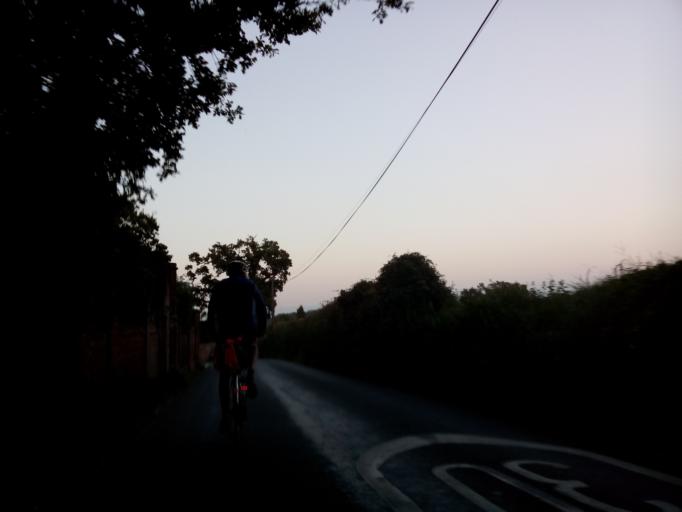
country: GB
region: England
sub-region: Suffolk
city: Kesgrave
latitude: 52.0922
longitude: 1.2457
